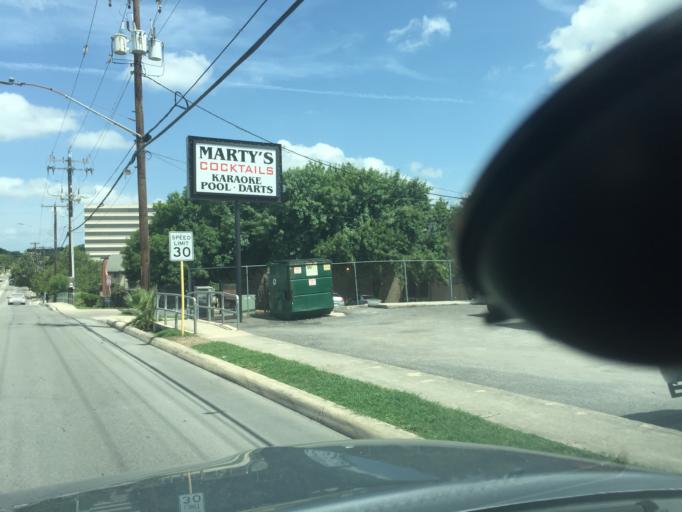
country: US
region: Texas
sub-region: Bexar County
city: Castle Hills
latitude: 29.5288
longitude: -98.4933
